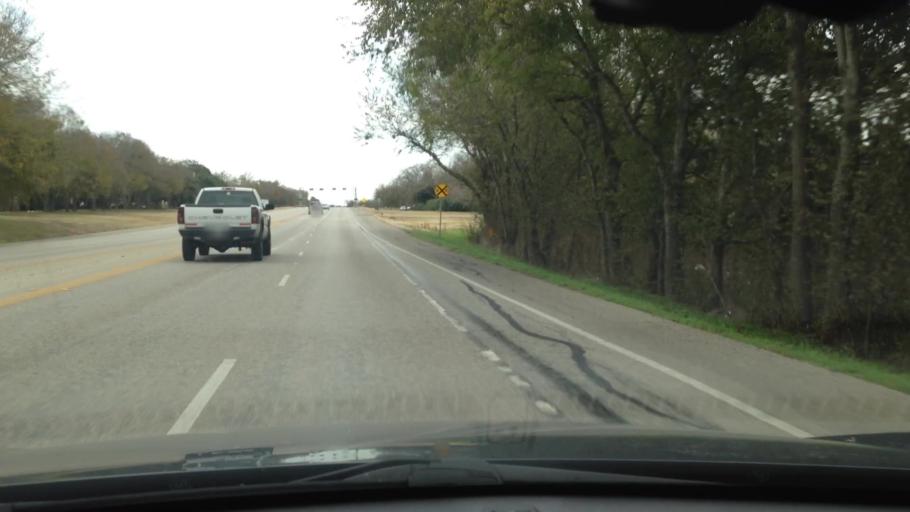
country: US
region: Texas
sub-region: Hays County
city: San Marcos
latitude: 29.8804
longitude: -97.8987
